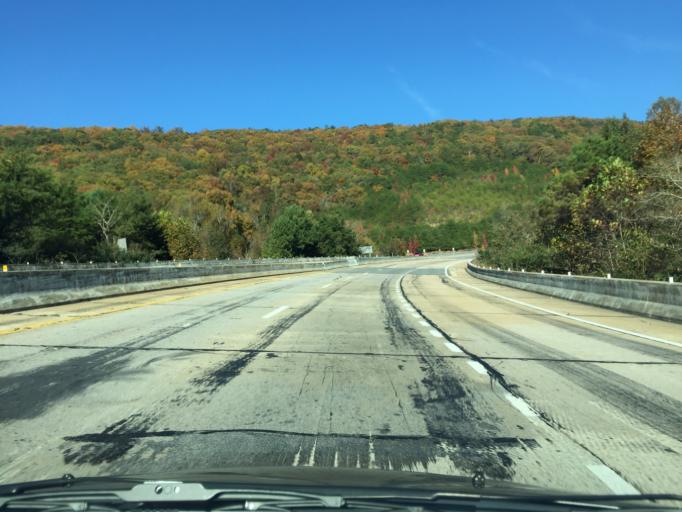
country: US
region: Tennessee
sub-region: Hamilton County
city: Soddy-Daisy
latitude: 35.3048
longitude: -85.1631
